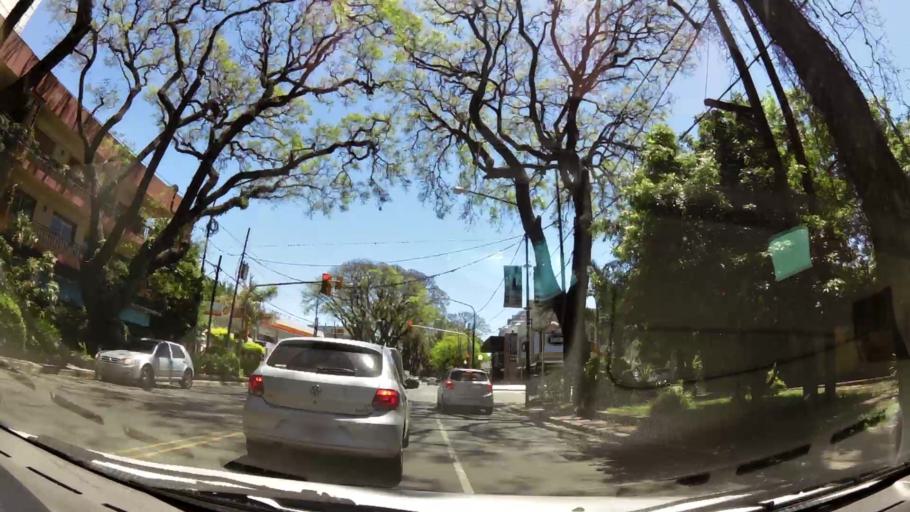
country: AR
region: Buenos Aires
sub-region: Partido de San Isidro
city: San Isidro
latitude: -34.4828
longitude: -58.4902
